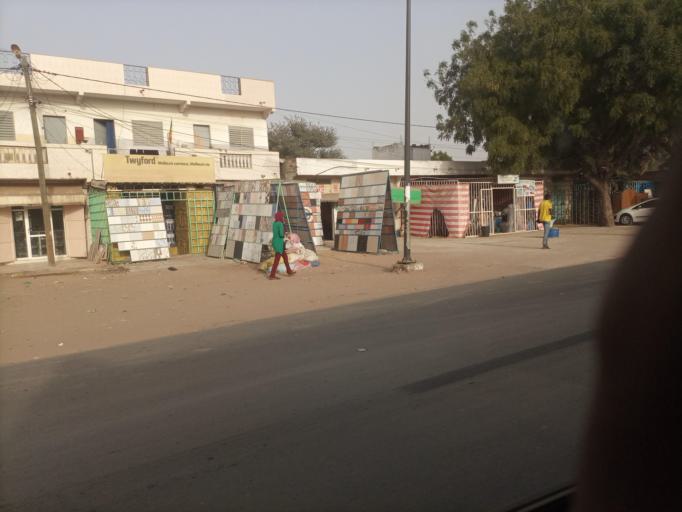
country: SN
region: Thies
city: Warang
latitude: 14.4383
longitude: -16.9779
